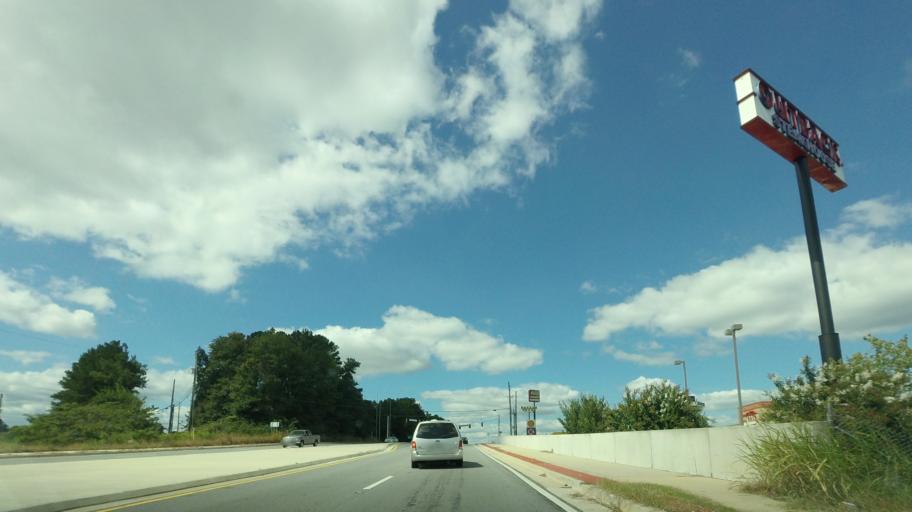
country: US
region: Georgia
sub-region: Bibb County
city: Macon
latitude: 32.9041
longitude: -83.6866
